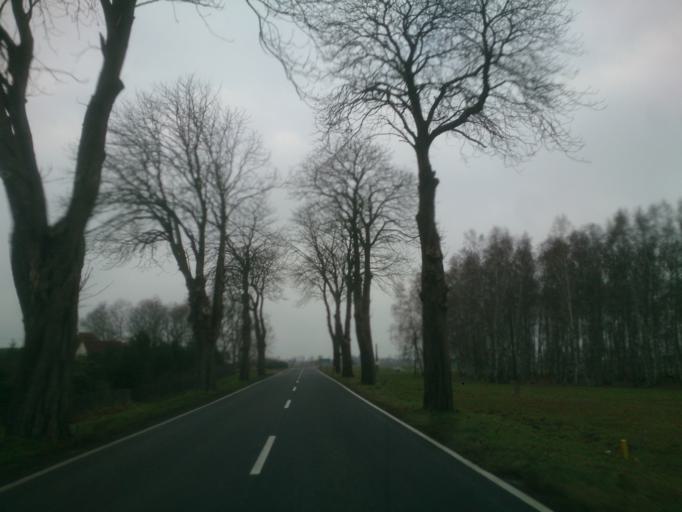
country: PL
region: West Pomeranian Voivodeship
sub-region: Powiat slawienski
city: Darlowo
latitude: 54.4027
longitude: 16.4153
